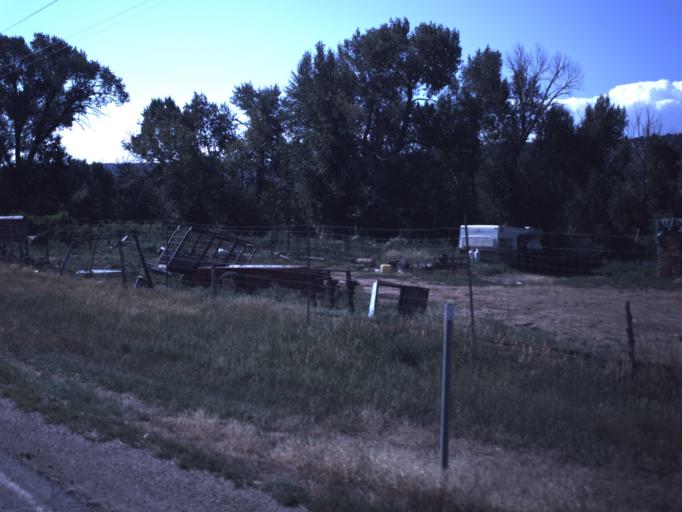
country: US
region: Utah
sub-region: Duchesne County
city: Duchesne
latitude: 40.3456
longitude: -110.6999
